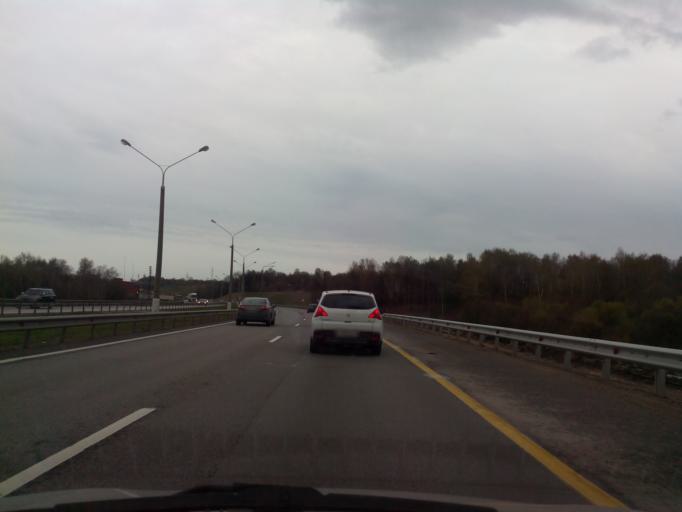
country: RU
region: Moskovskaya
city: Stupino
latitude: 54.8219
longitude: 38.0420
